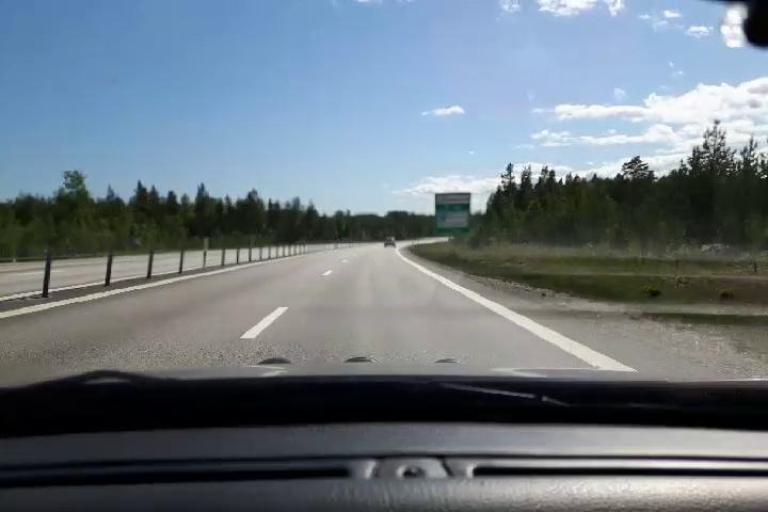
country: SE
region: Gaevleborg
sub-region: Hudiksvalls Kommun
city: Iggesund
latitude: 61.6919
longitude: 17.0563
